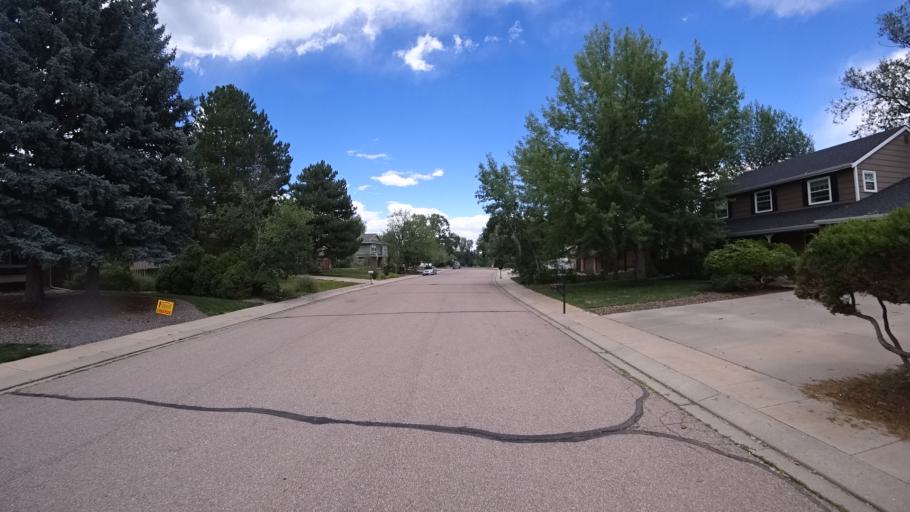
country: US
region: Colorado
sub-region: El Paso County
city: Colorado Springs
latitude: 38.7901
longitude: -104.8316
